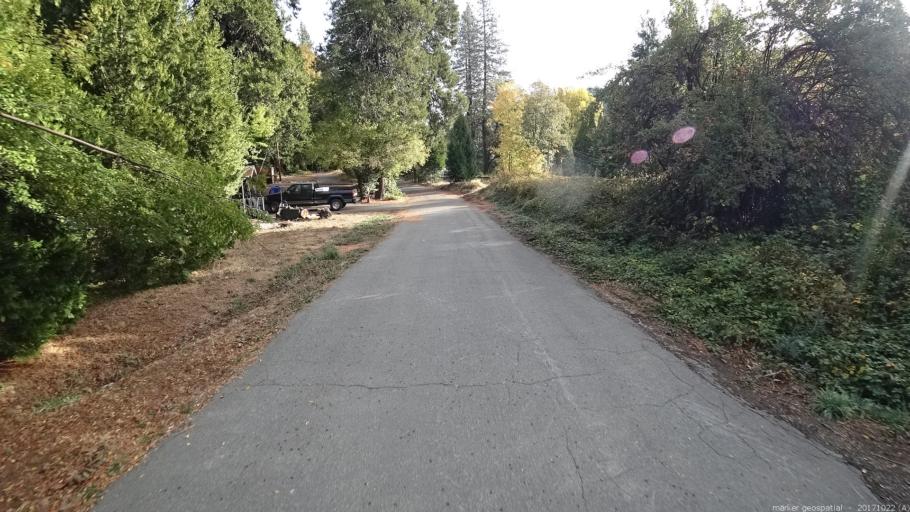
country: US
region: California
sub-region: Siskiyou County
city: Dunsmuir
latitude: 41.1375
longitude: -122.3200
